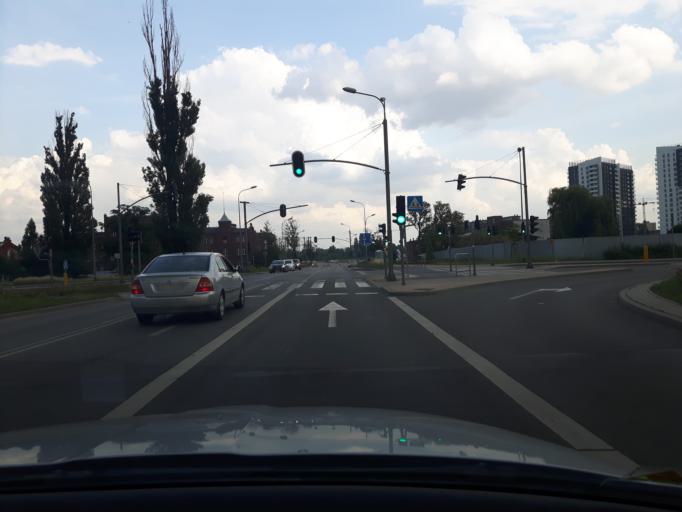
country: PL
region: Pomeranian Voivodeship
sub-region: Gdansk
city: Gdansk
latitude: 54.3628
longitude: 18.6503
